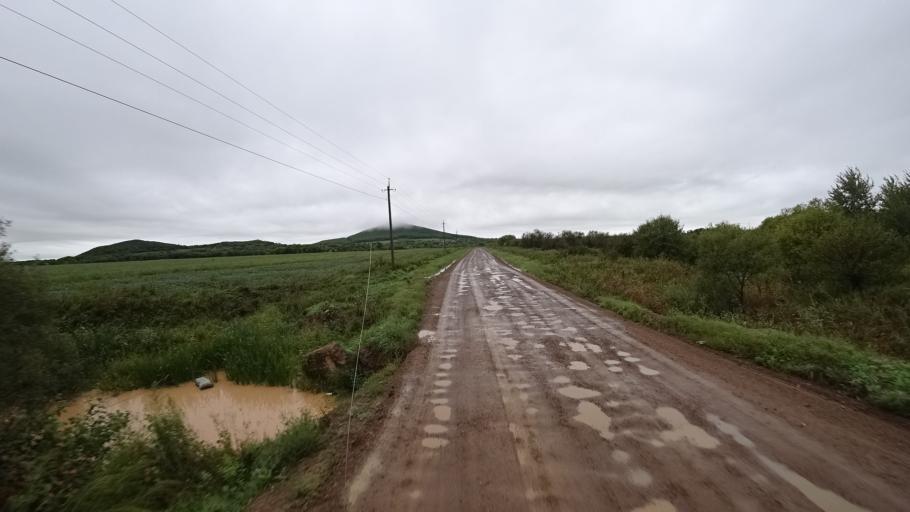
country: RU
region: Primorskiy
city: Monastyrishche
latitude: 44.2491
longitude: 132.4354
